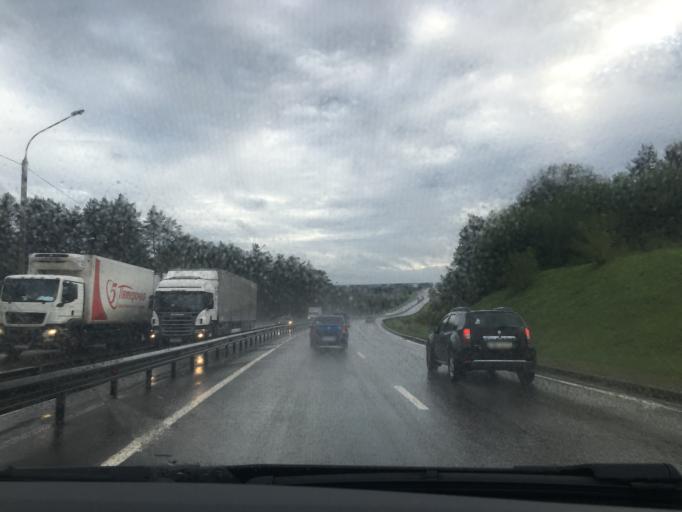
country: RU
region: Kaluga
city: Obninsk
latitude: 55.0552
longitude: 36.6175
